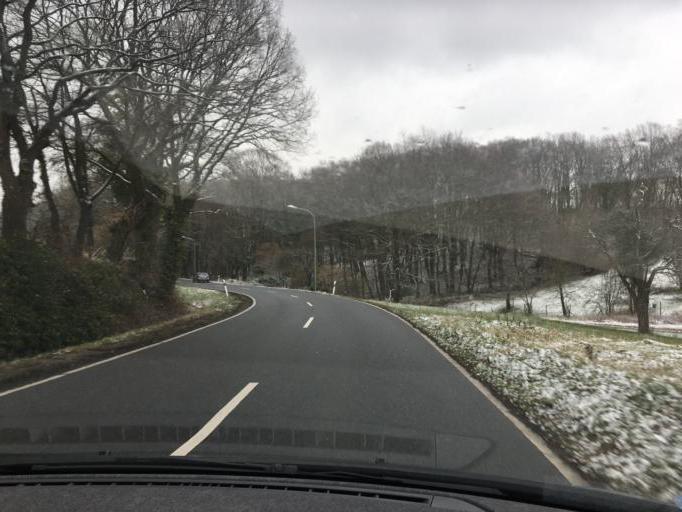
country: DE
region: North Rhine-Westphalia
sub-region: Regierungsbezirk Koln
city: Kreuzau
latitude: 50.7390
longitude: 6.4691
